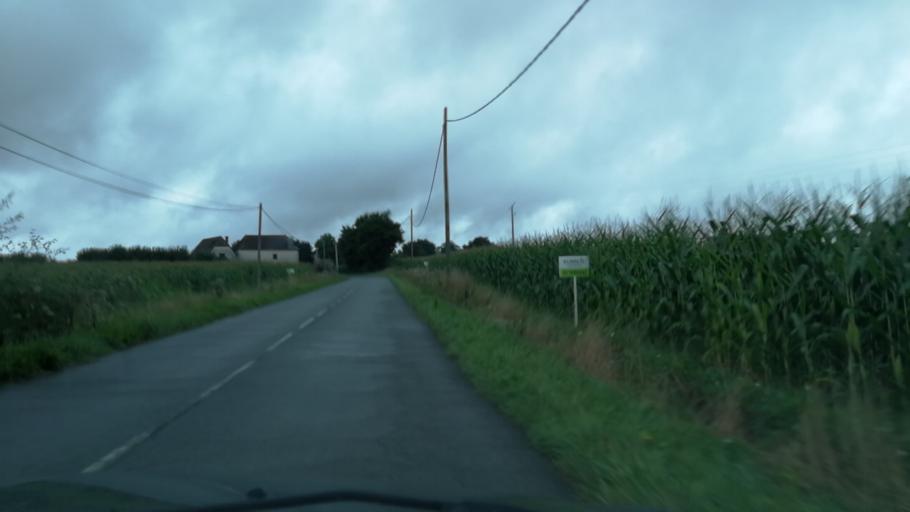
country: FR
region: Aquitaine
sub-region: Departement des Pyrenees-Atlantiques
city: Lucq-de-Bearn
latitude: 43.2923
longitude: -0.6711
